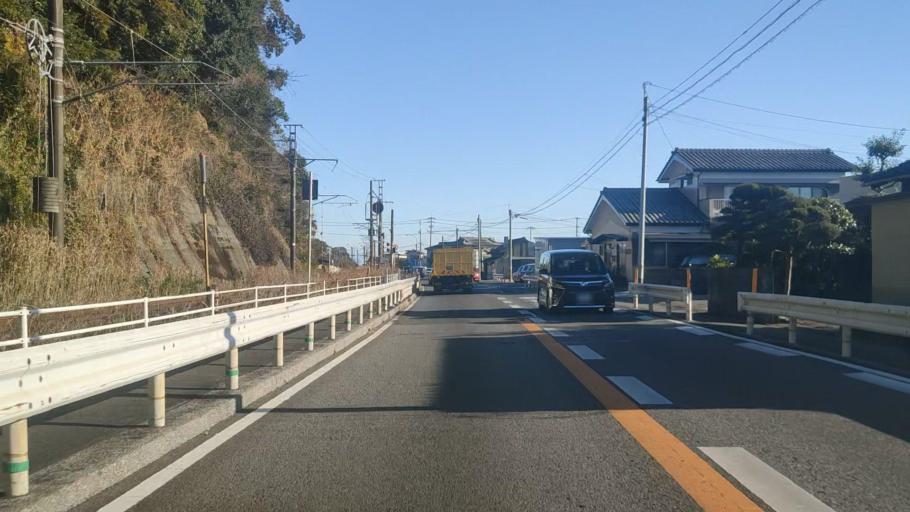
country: JP
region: Miyazaki
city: Nobeoka
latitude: 32.5106
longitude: 131.6796
